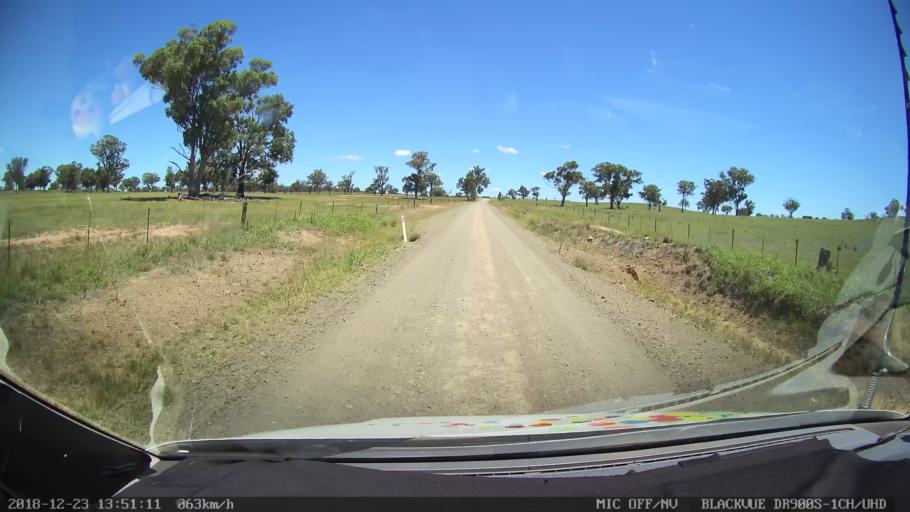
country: AU
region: New South Wales
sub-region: Tamworth Municipality
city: Manilla
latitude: -30.5374
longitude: 151.1055
